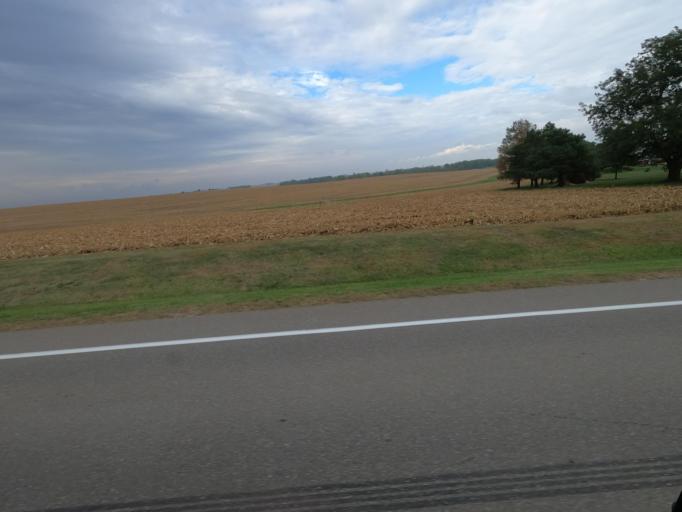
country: US
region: Iowa
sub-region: Henry County
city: Mount Pleasant
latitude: 40.7845
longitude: -91.5827
